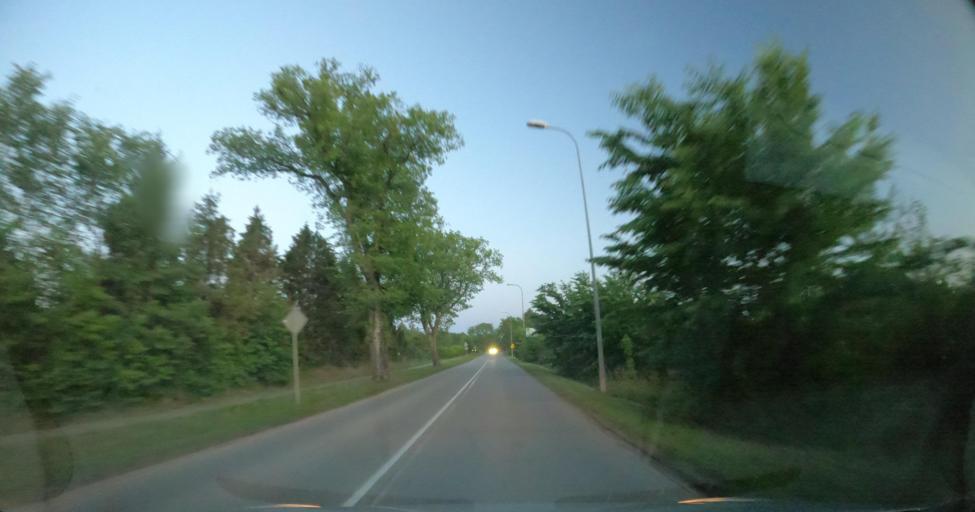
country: PL
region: Pomeranian Voivodeship
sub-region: Powiat wejherowski
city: Szemud
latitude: 54.4765
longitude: 18.2708
